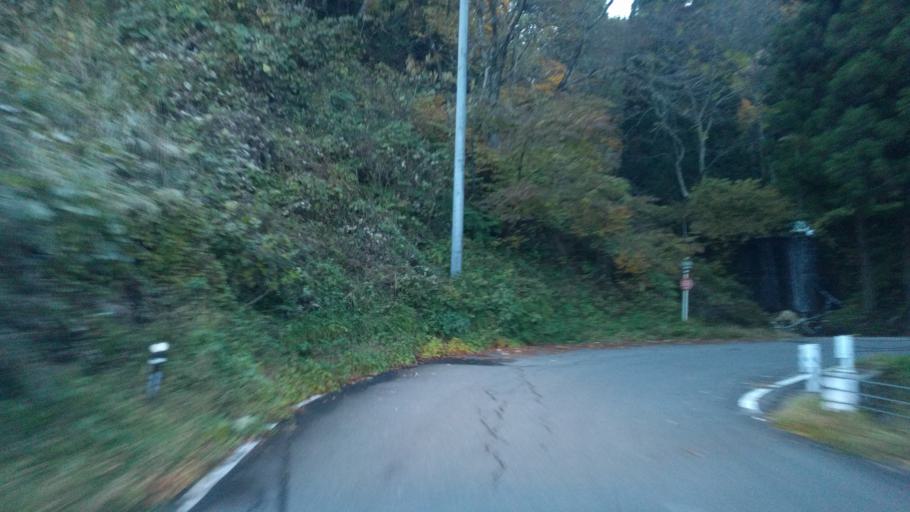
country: JP
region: Fukushima
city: Kitakata
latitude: 37.5228
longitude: 139.7065
